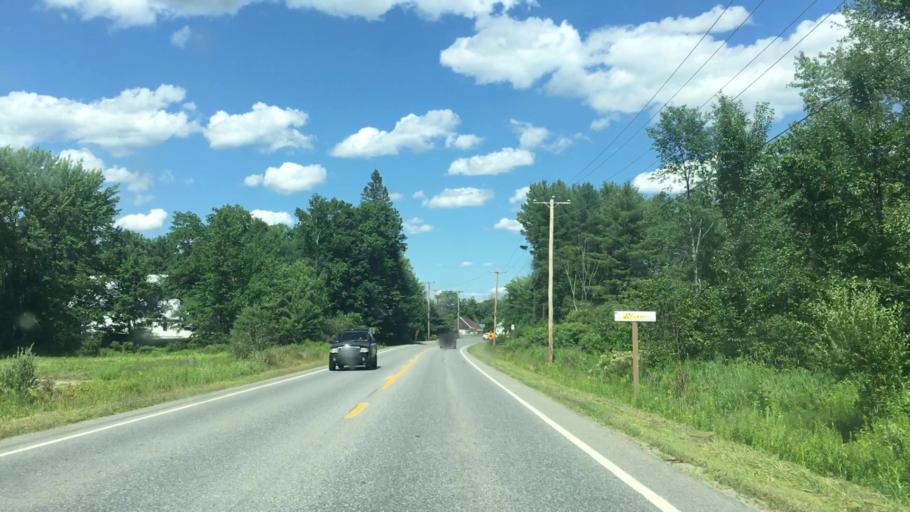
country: US
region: Maine
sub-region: Franklin County
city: New Sharon
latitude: 44.6180
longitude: -70.0771
